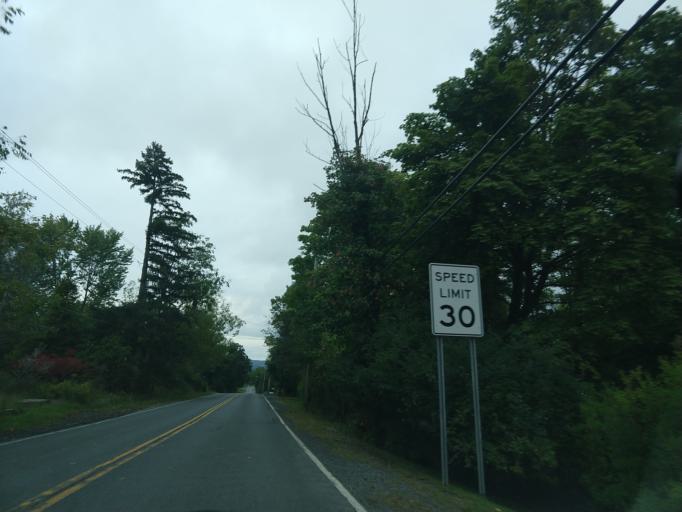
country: US
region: New York
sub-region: Tompkins County
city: South Hill
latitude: 42.4232
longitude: -76.4852
